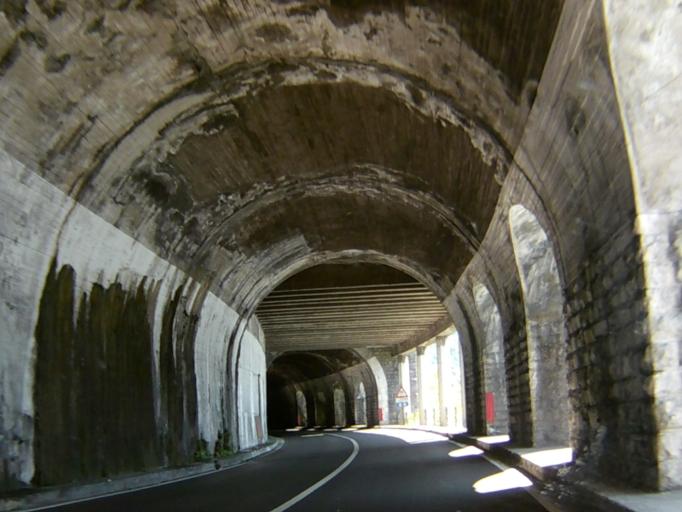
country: IT
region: Lombardy
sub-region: Provincia di Lecco
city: Lierna
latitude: 45.9452
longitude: 9.3068
